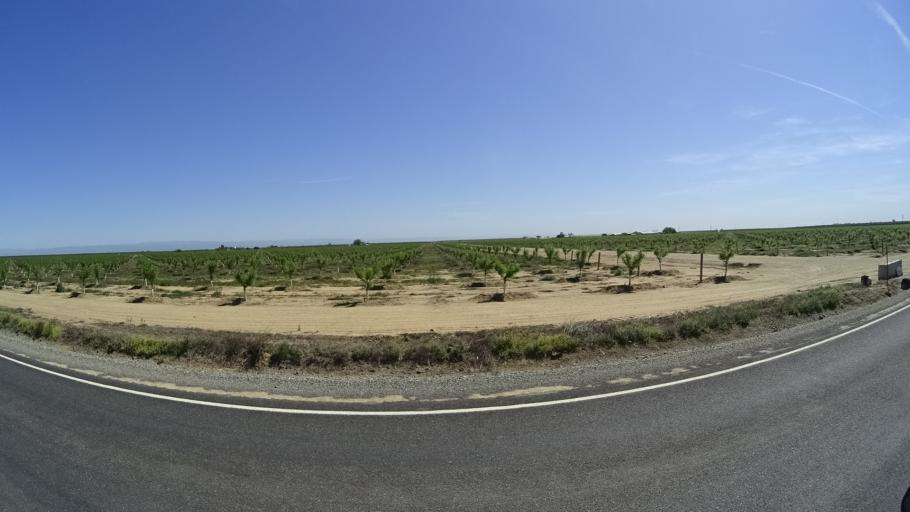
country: US
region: California
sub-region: Glenn County
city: Orland
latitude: 39.6457
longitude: -122.1410
